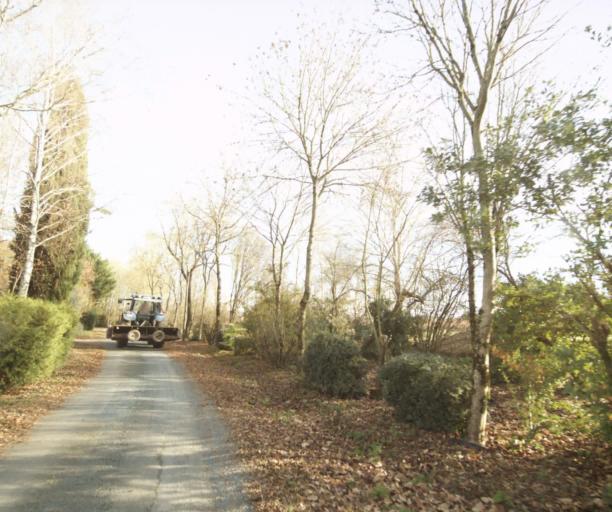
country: FR
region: Poitou-Charentes
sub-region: Departement de la Charente-Maritime
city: Chaniers
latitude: 45.7357
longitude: -0.5207
